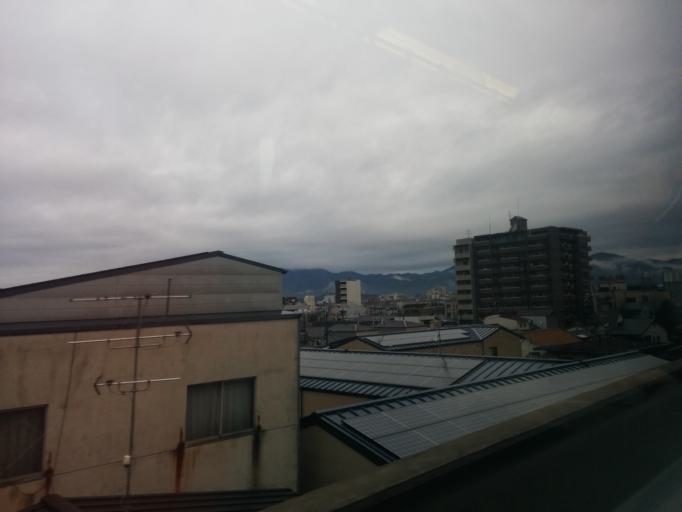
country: JP
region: Kyoto
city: Kyoto
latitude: 35.0020
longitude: 135.7416
